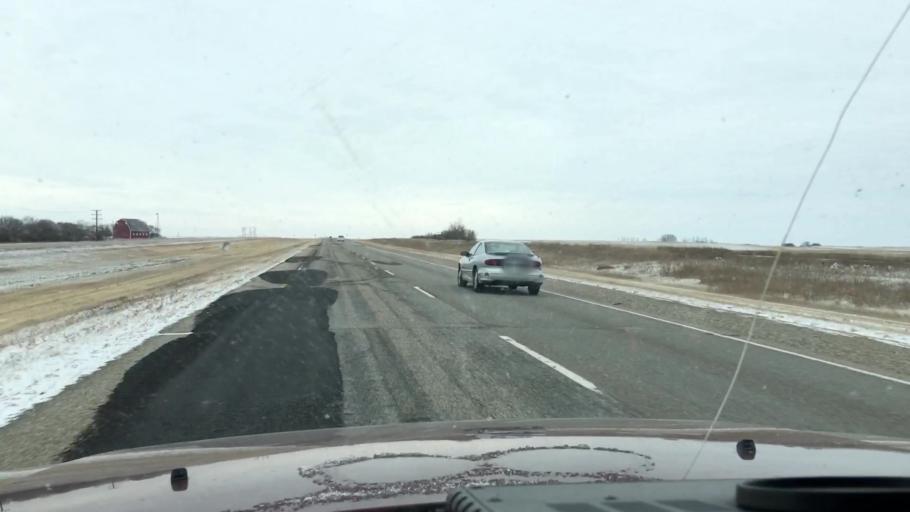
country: CA
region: Saskatchewan
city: Watrous
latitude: 51.4221
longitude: -106.1944
